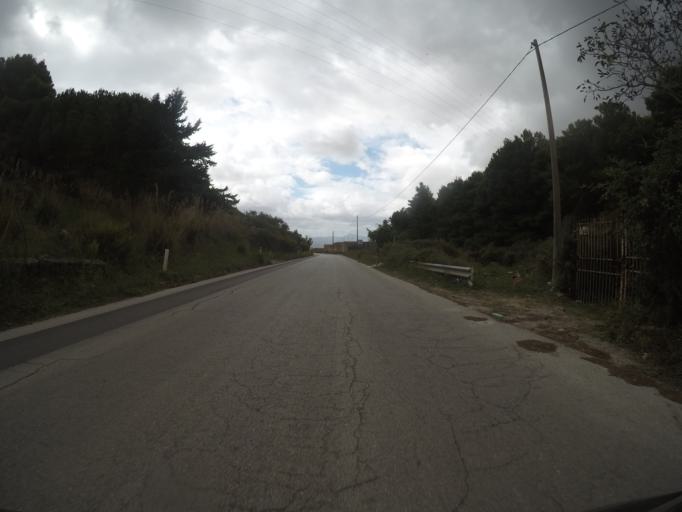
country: IT
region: Sicily
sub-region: Palermo
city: Montelepre
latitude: 38.1001
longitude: 13.1696
